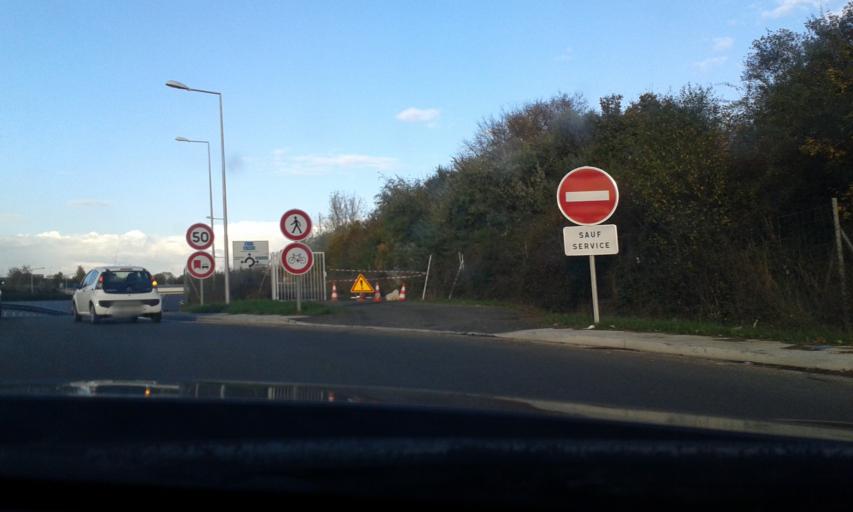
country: FR
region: Centre
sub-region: Departement d'Eure-et-Loir
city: Le Coudray
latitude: 48.4249
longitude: 1.5134
